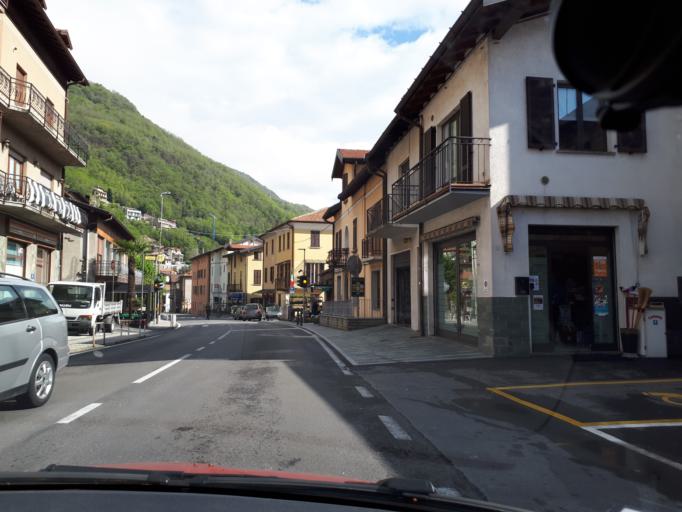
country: IT
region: Lombardy
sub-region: Provincia di Como
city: San Siro
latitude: 46.0538
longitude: 9.2590
